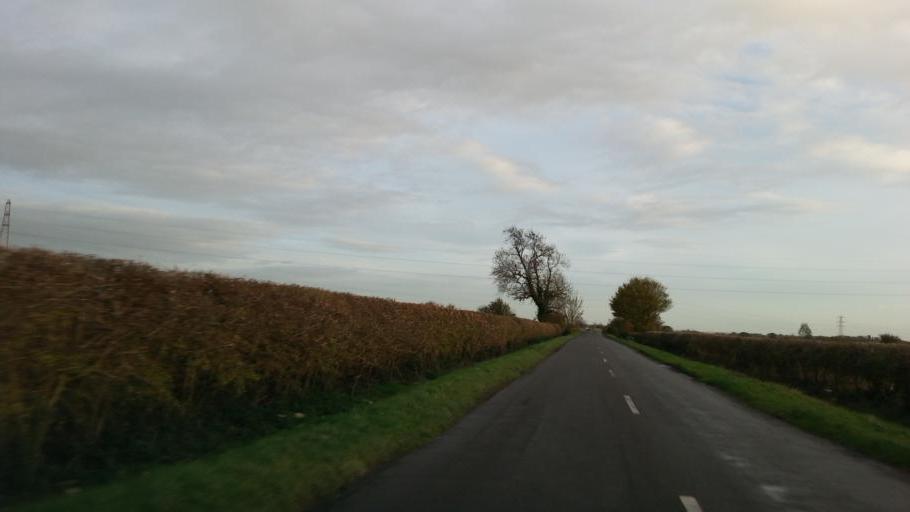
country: GB
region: England
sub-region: Nottinghamshire
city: Farndon
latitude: 53.0144
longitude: -0.8571
